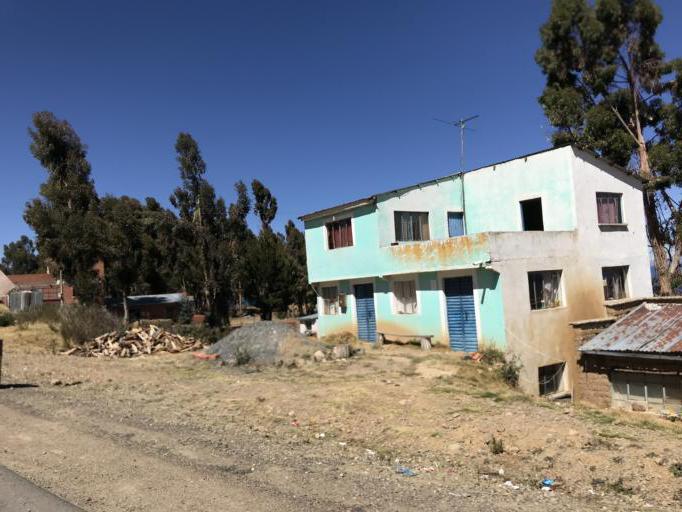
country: BO
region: La Paz
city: Huatajata
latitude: -16.2156
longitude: -68.6652
